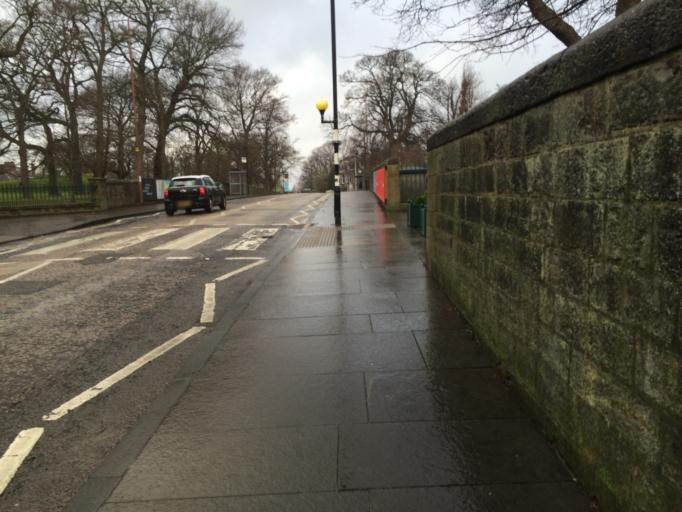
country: GB
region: Scotland
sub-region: Edinburgh
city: Edinburgh
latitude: 55.9511
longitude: -3.2250
